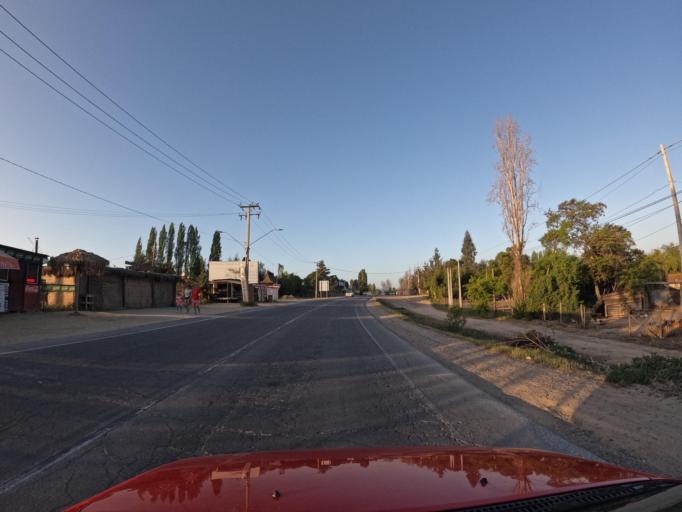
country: CL
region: O'Higgins
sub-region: Provincia de Cachapoal
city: San Vicente
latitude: -34.1669
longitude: -71.3964
